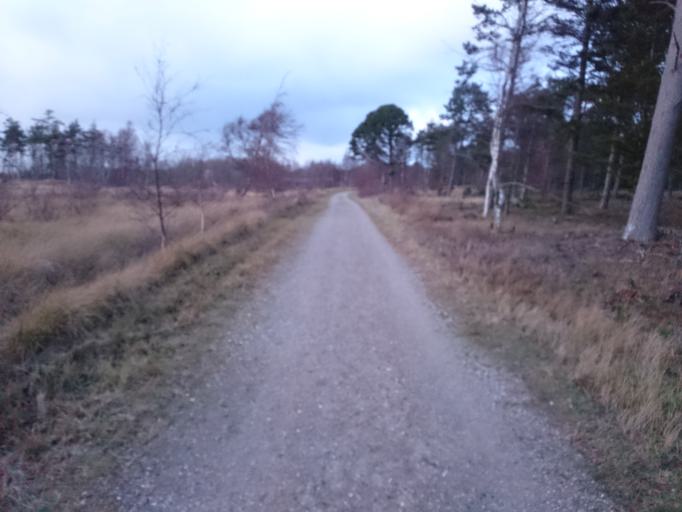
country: DK
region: North Denmark
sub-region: Frederikshavn Kommune
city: Skagen
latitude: 57.7127
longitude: 10.5449
